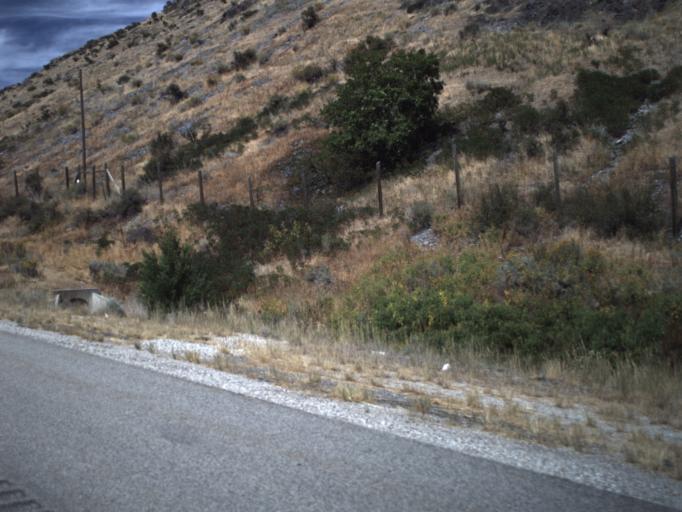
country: US
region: Utah
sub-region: Box Elder County
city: Brigham City
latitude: 41.5203
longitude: -111.9421
